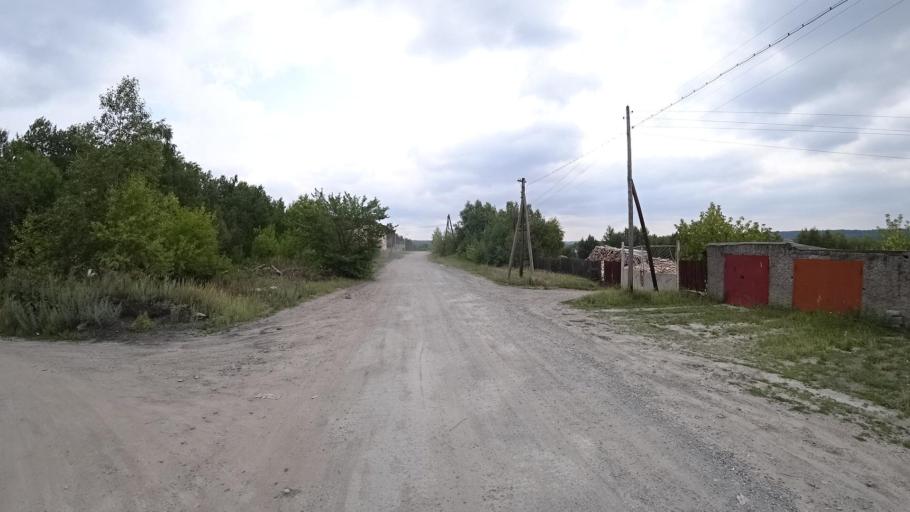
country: RU
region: Sverdlovsk
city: Kamyshlov
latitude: 56.8301
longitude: 62.7276
